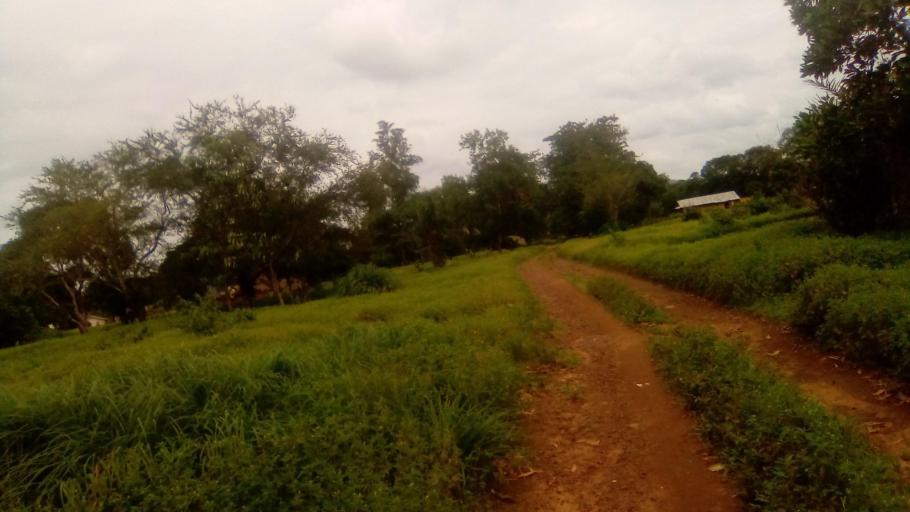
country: SL
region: Southern Province
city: Moyamba
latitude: 8.1568
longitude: -12.4203
